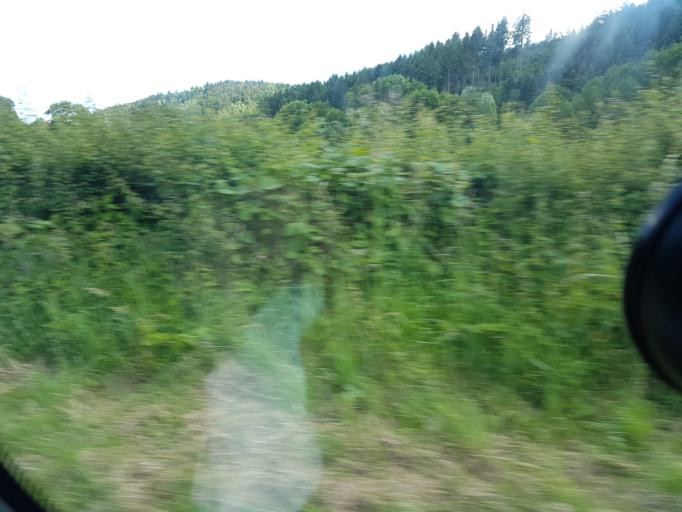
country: FR
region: Bourgogne
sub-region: Departement de la Cote-d'Or
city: Saulieu
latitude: 47.1437
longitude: 4.2073
